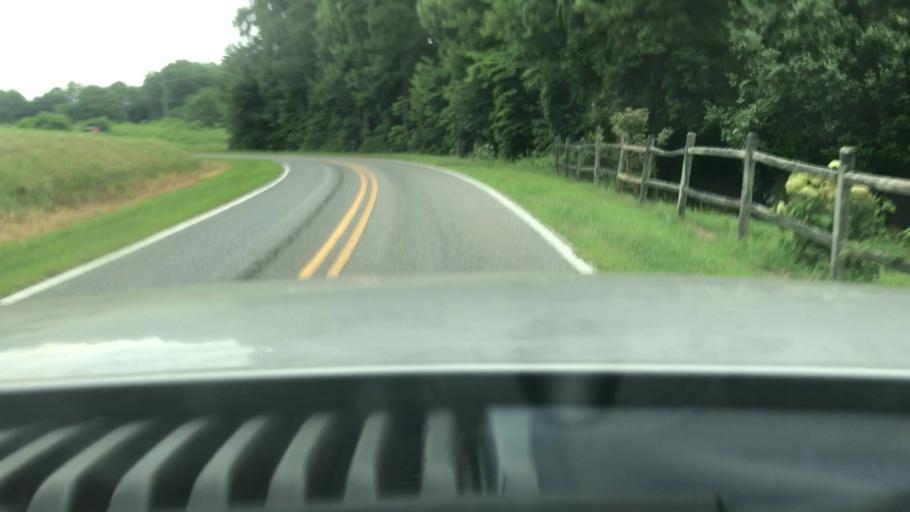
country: US
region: North Carolina
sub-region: Surry County
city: Thurmond
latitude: 36.4183
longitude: -80.8317
